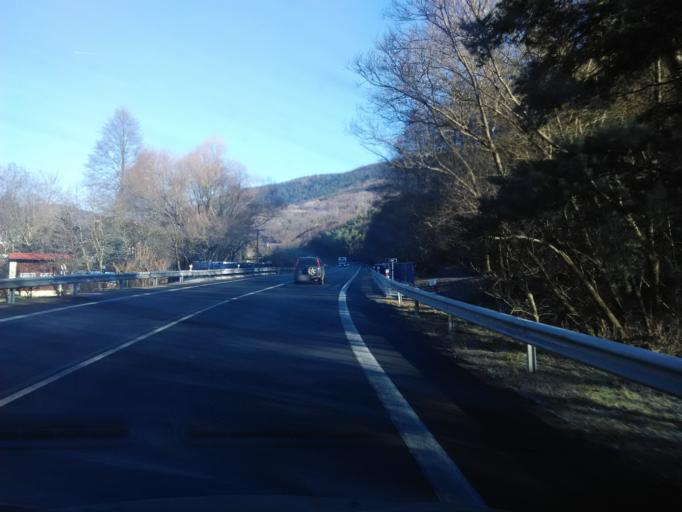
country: SK
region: Banskobystricky
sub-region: Okres Ziar nad Hronom
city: Kremnica
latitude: 48.6763
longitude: 18.9118
